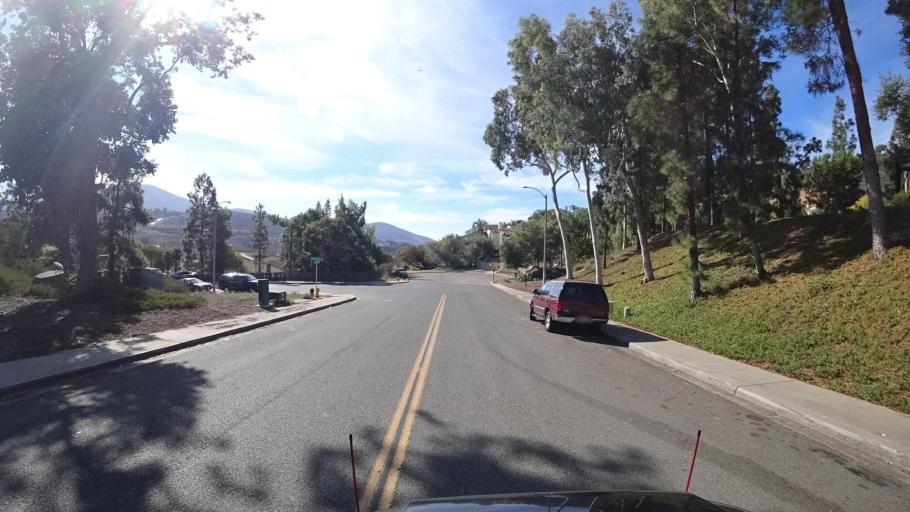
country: US
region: California
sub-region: San Diego County
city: Spring Valley
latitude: 32.7286
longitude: -116.9739
